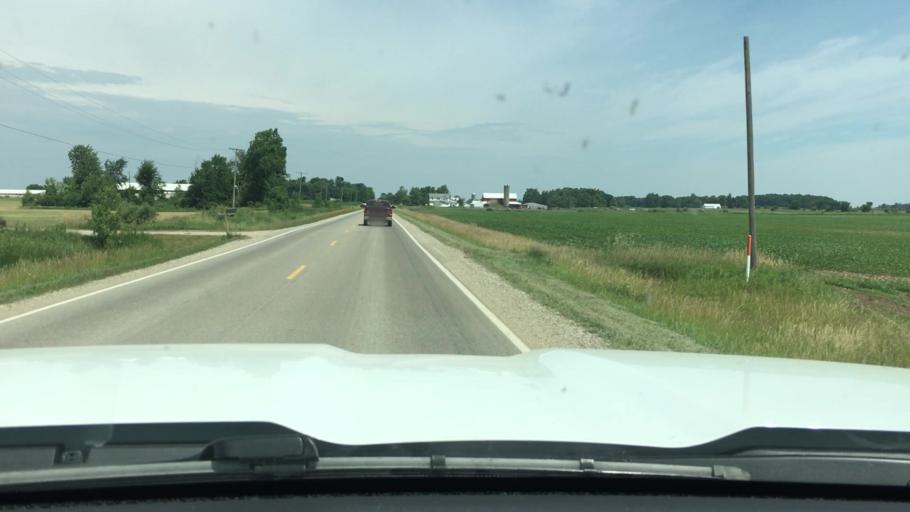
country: US
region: Michigan
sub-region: Sanilac County
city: Brown City
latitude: 43.2887
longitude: -82.9829
